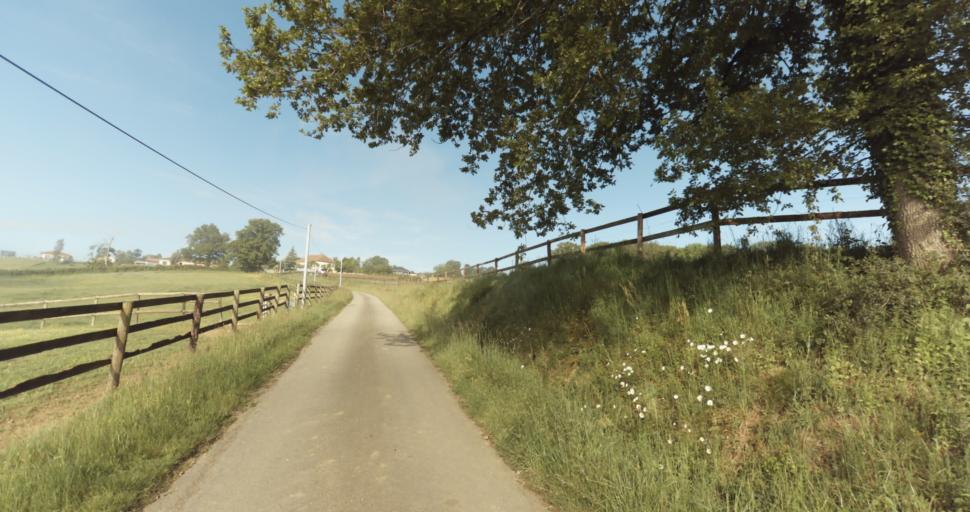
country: FR
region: Limousin
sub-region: Departement de la Haute-Vienne
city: Solignac
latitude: 45.7464
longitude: 1.2787
